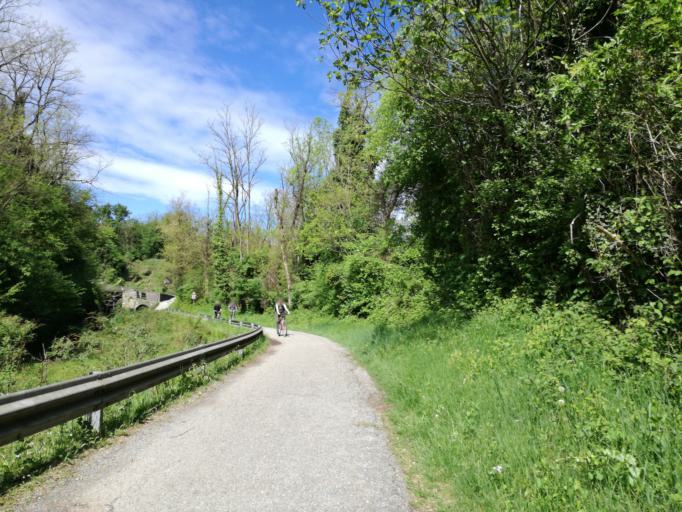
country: IT
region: Lombardy
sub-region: Provincia di Bergamo
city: Calusco d'Adda
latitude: 45.6762
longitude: 9.4665
